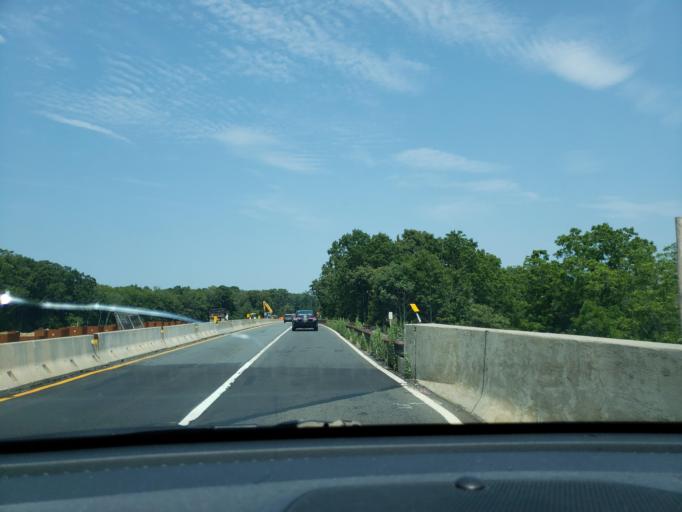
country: US
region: New Jersey
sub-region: Atlantic County
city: Linwood
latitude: 39.3489
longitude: -74.5982
